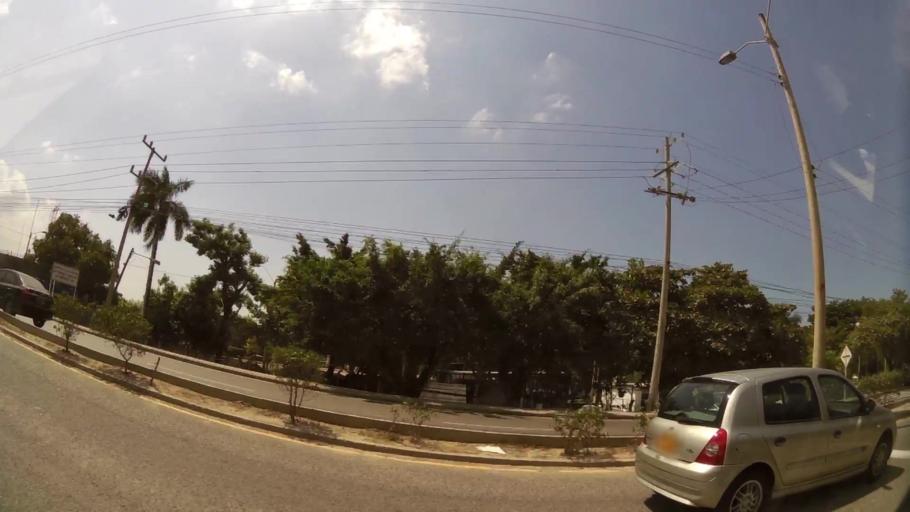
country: CO
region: Bolivar
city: Cartagena
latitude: 10.3589
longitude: -75.5057
